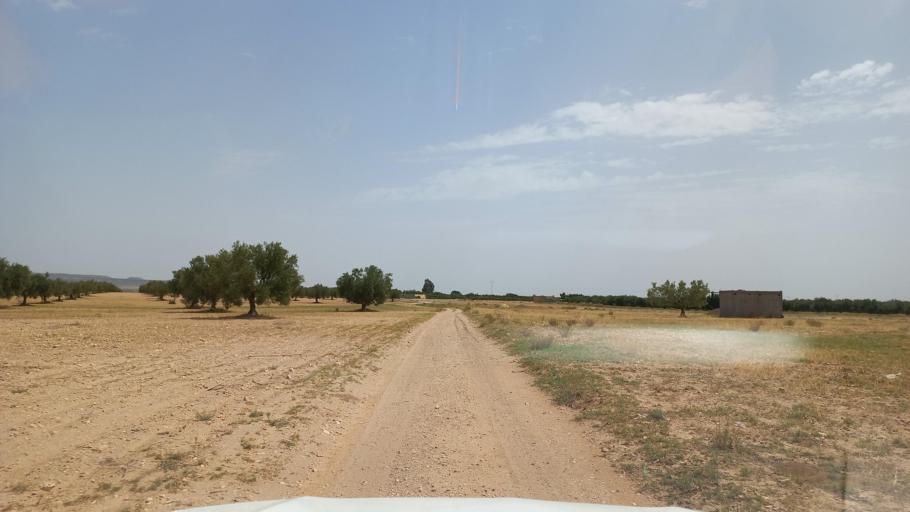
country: TN
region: Al Qasrayn
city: Kasserine
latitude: 35.2876
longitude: 9.0313
